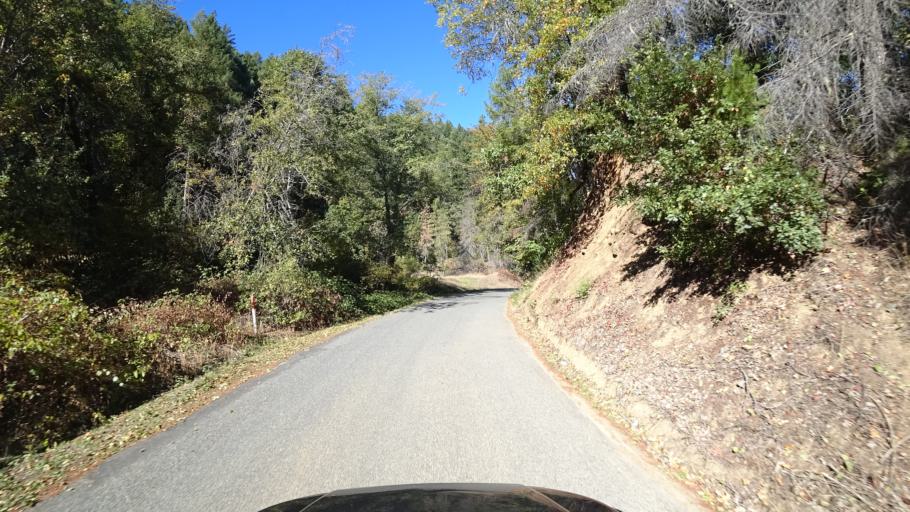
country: US
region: California
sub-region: Humboldt County
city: Willow Creek
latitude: 41.2450
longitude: -123.2990
